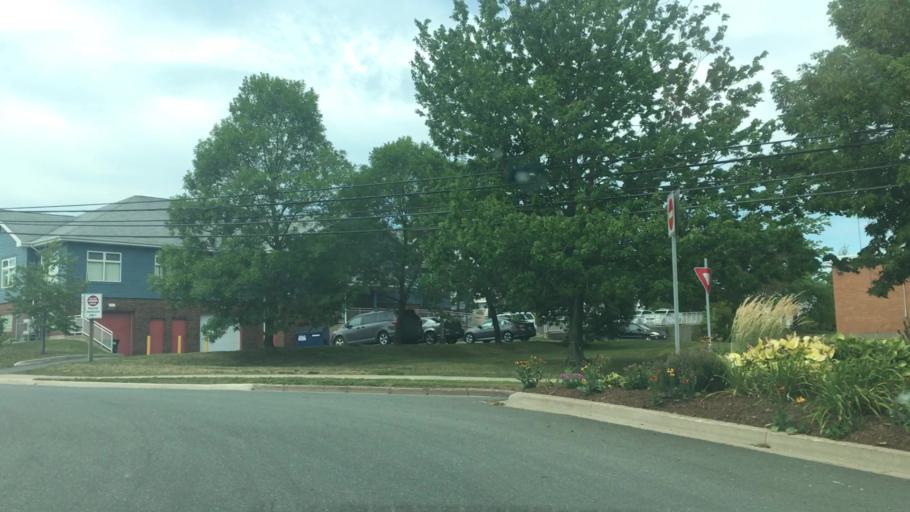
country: CA
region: Nova Scotia
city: Antigonish
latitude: 45.6166
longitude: -61.9992
